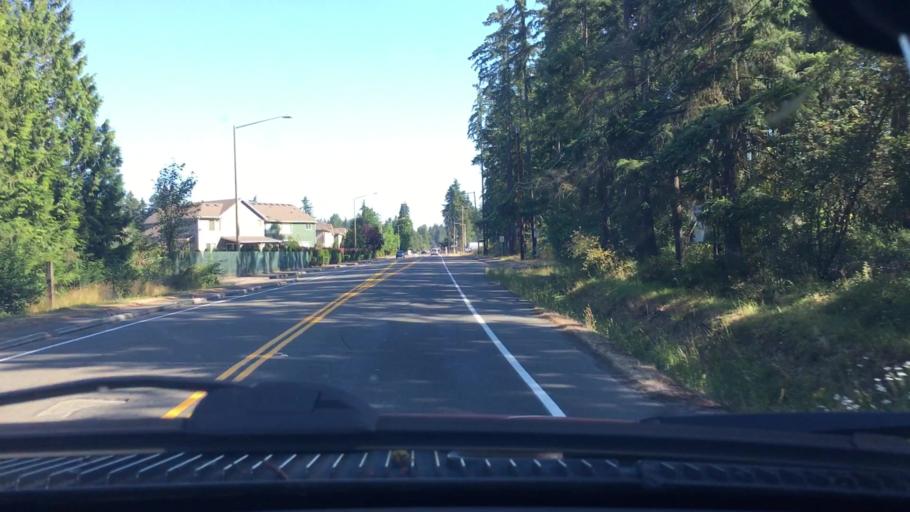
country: US
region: Washington
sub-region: King County
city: Covington
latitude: 47.3487
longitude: -122.1389
